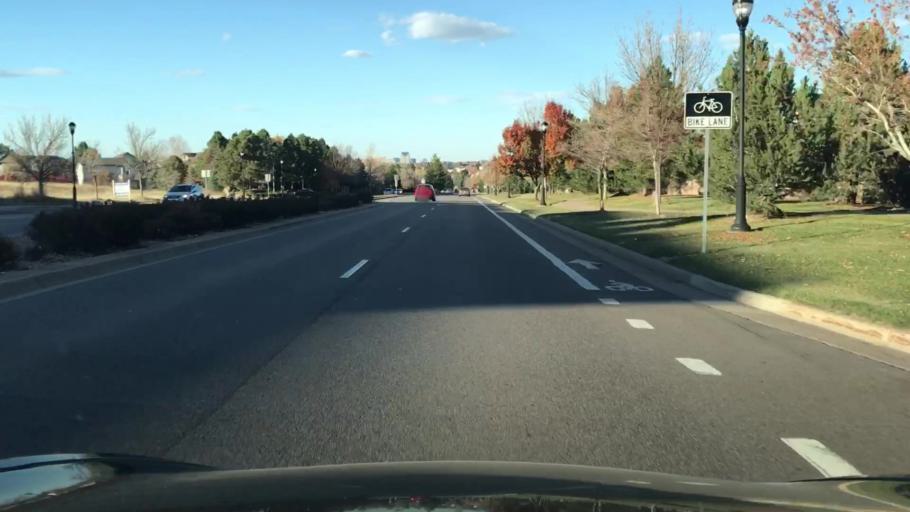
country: US
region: Colorado
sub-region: Adams County
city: Lone Tree
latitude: 39.5405
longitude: -104.8855
